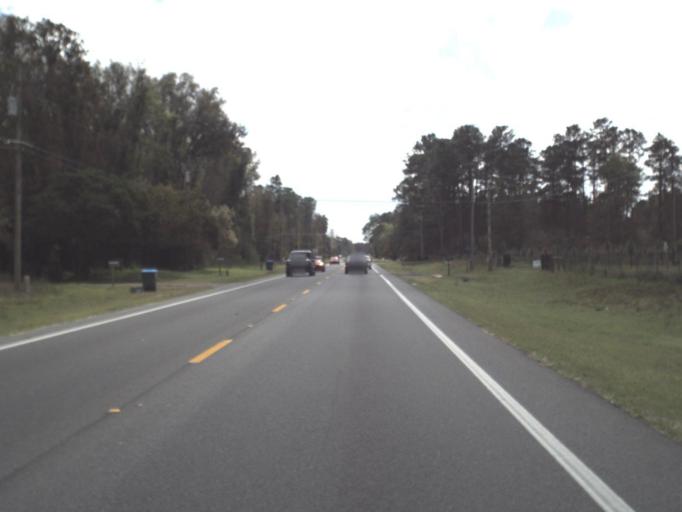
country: US
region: Florida
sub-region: Wakulla County
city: Crawfordville
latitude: 30.2290
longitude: -84.3624
